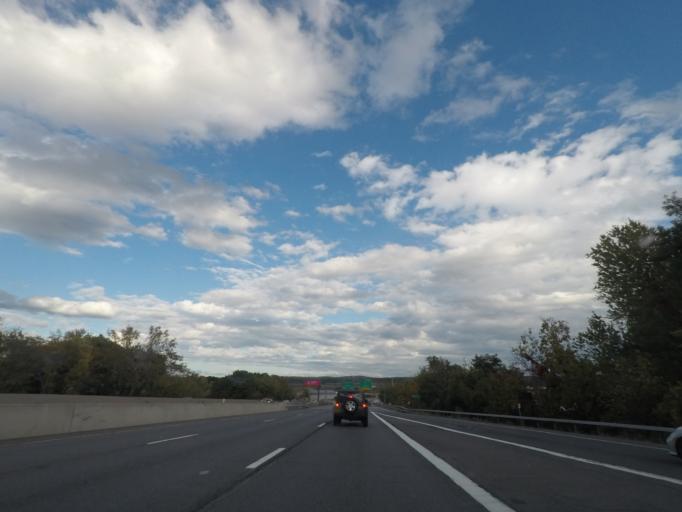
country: US
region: New York
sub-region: Albany County
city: Albany
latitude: 42.6699
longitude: -73.7428
